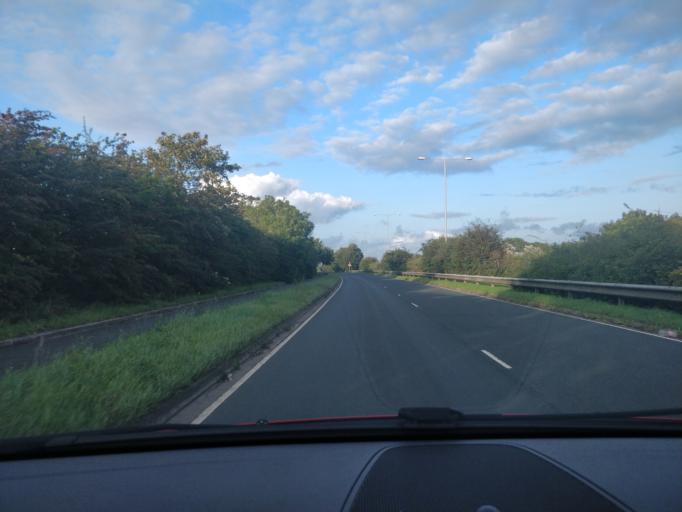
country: GB
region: England
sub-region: Lancashire
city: Tarleton
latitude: 53.6648
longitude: -2.8705
